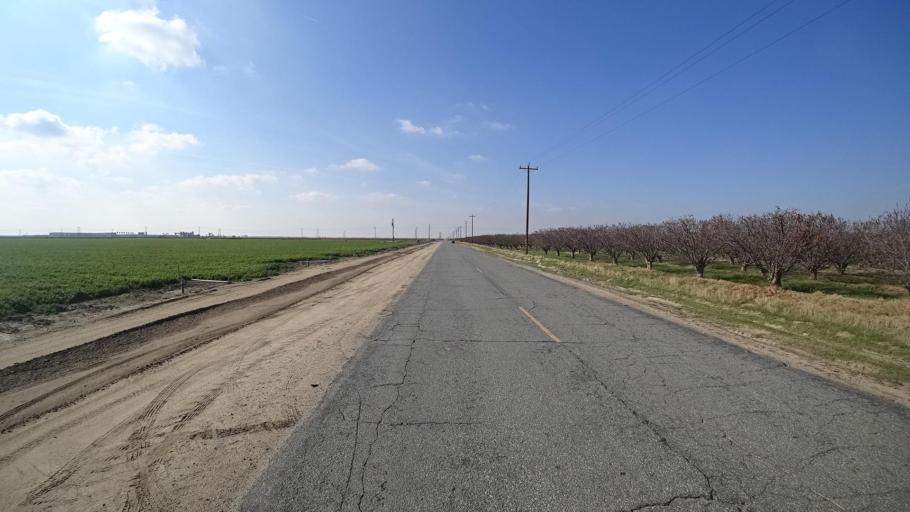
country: US
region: California
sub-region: Kern County
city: Arvin
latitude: 35.2674
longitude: -118.8216
